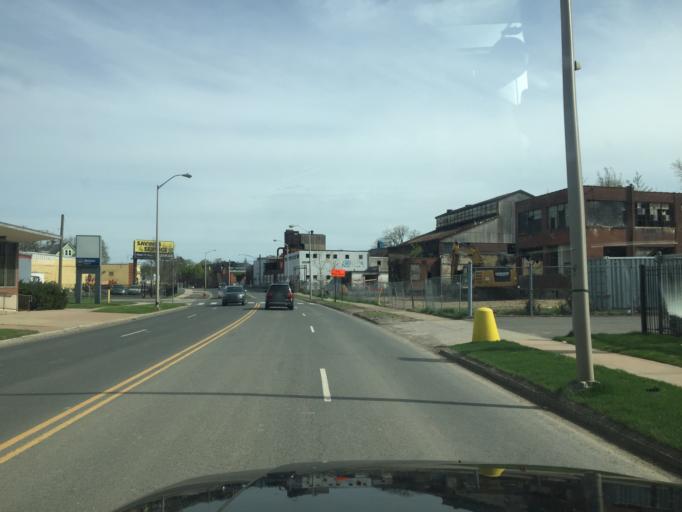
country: US
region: Connecticut
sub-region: Hartford County
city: Hartford
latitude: 41.7824
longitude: -72.7027
